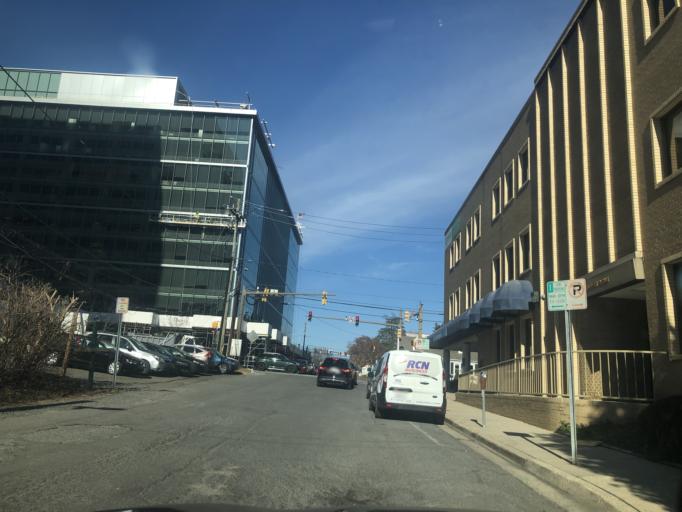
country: US
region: Maryland
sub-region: Montgomery County
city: Bethesda
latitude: 38.9836
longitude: -77.0907
